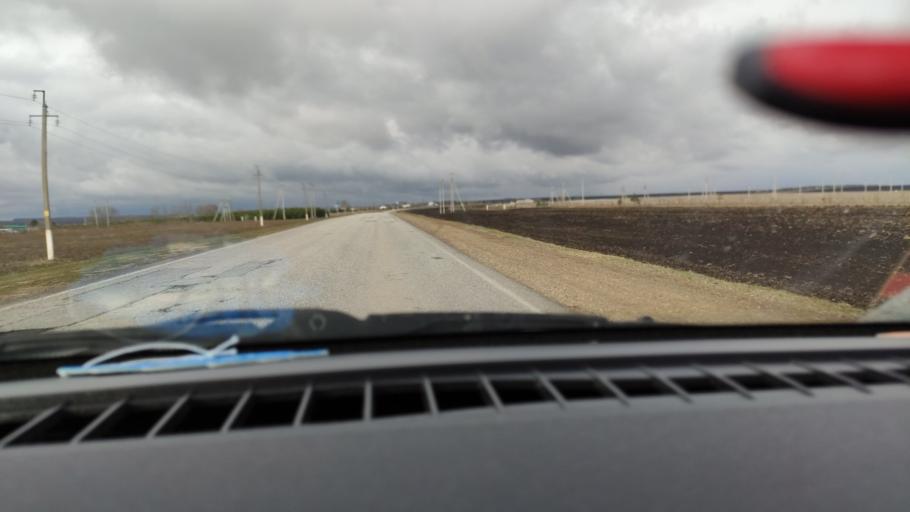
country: RU
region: Tatarstan
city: Cheremshan
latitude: 54.8315
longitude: 51.5625
